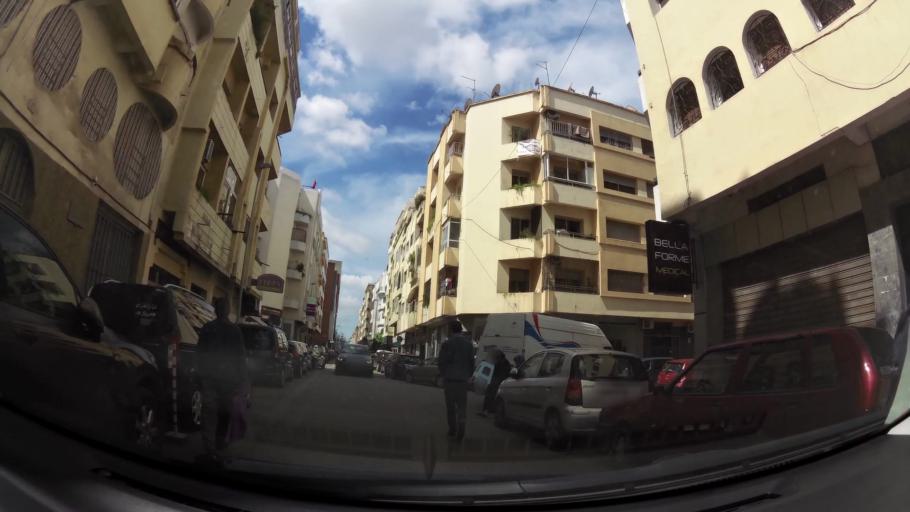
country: MA
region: Grand Casablanca
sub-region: Casablanca
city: Casablanca
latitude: 33.5762
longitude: -7.6452
